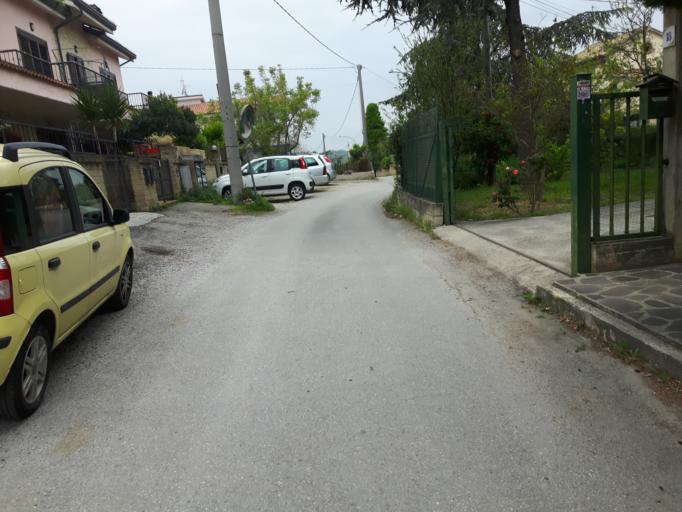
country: IT
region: Abruzzo
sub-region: Provincia di Chieti
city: Vasto
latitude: 42.1425
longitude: 14.6960
